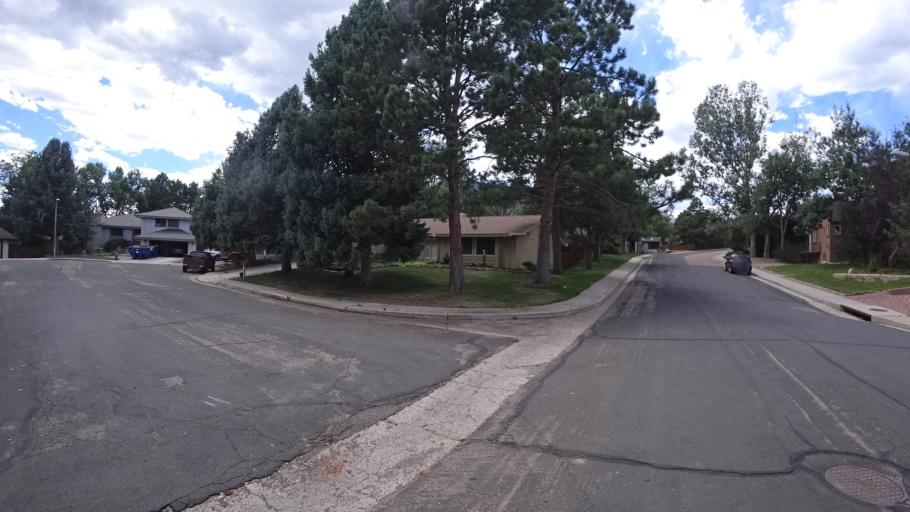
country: US
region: Colorado
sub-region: El Paso County
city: Stratmoor
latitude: 38.7828
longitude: -104.8287
